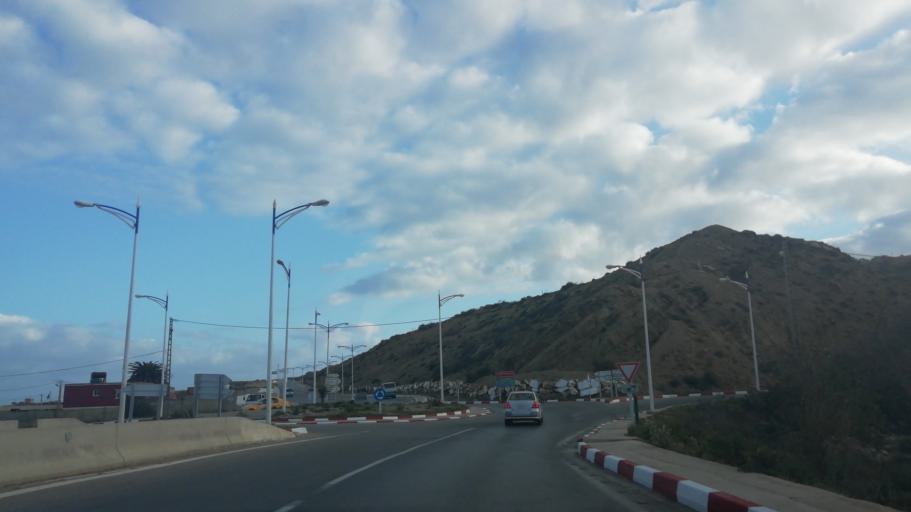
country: DZ
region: Mostaganem
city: Mostaganem
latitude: 36.0355
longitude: 0.1422
